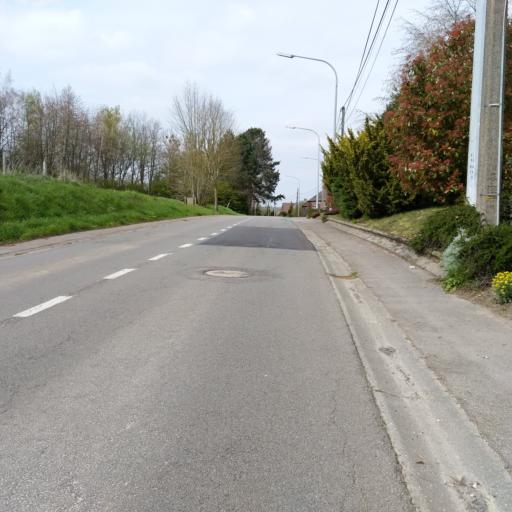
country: BE
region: Wallonia
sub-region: Province du Hainaut
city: Quevy-le-Petit
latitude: 50.3669
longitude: 3.9421
